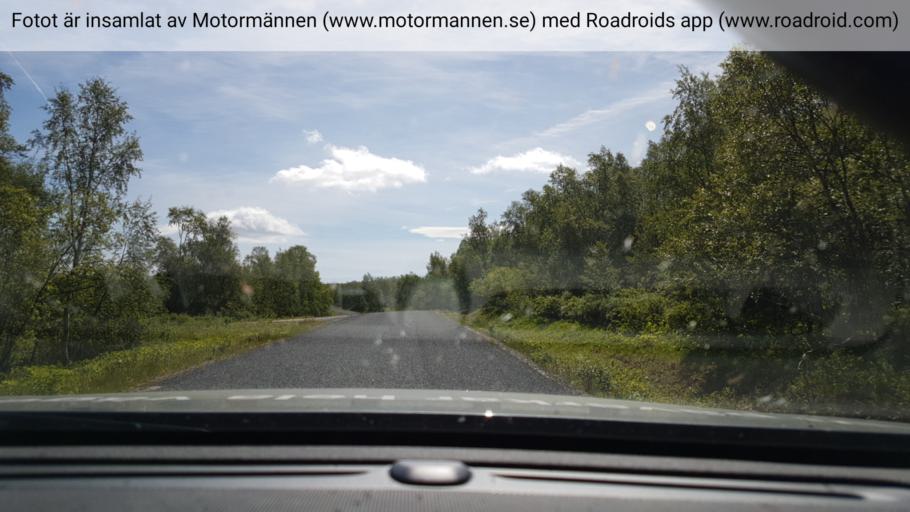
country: NO
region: Nordland
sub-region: Hattfjelldal
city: Hattfjelldal
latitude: 65.4202
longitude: 14.9169
